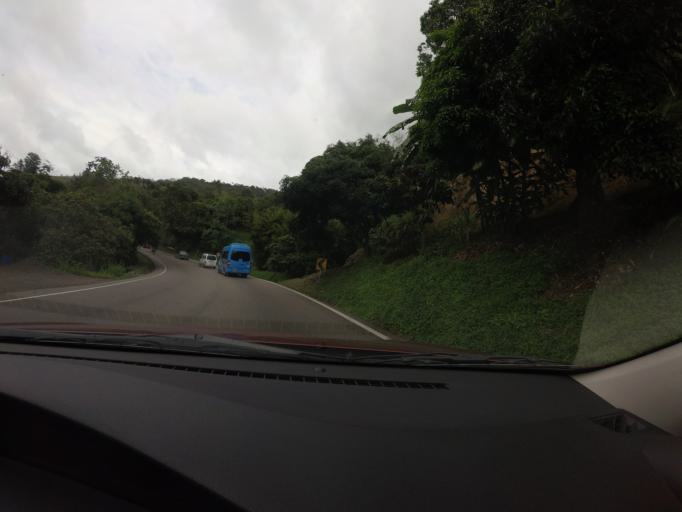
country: CO
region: Cundinamarca
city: Granada
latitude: 5.0637
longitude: -74.5736
